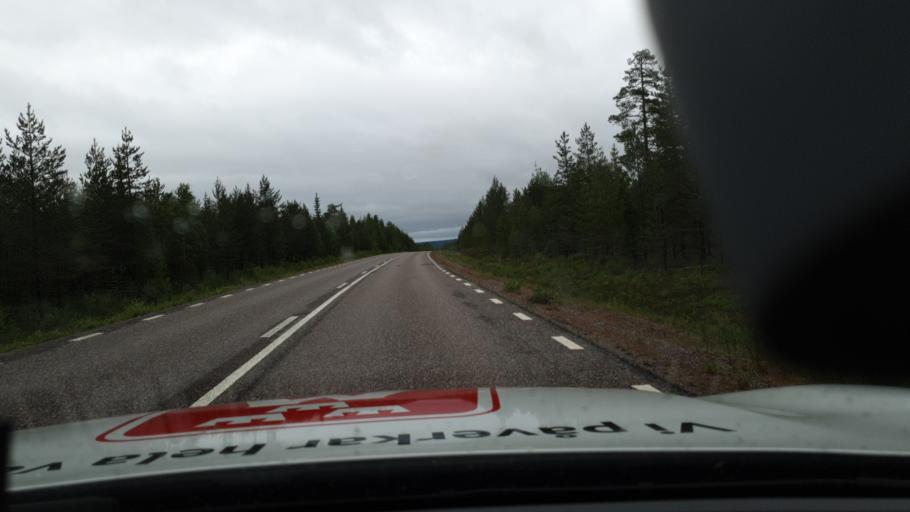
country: SE
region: Norrbotten
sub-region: Pajala Kommun
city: Pajala
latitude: 67.1762
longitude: 23.5033
